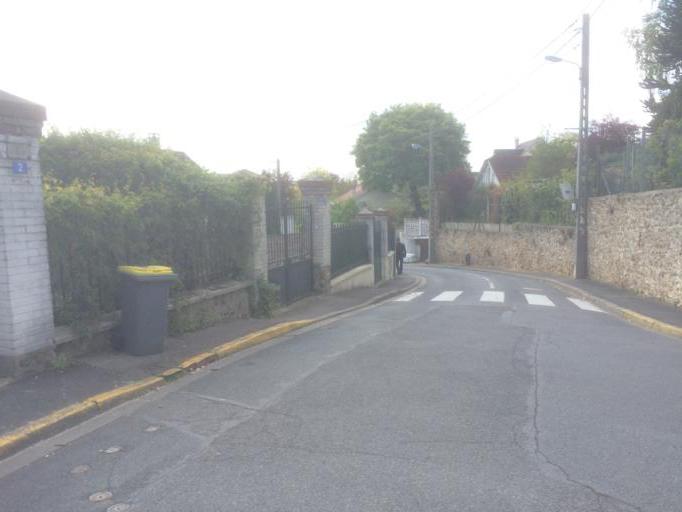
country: FR
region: Ile-de-France
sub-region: Departement de l'Essonne
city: Villebon-sur-Yvette
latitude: 48.7033
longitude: 2.2153
